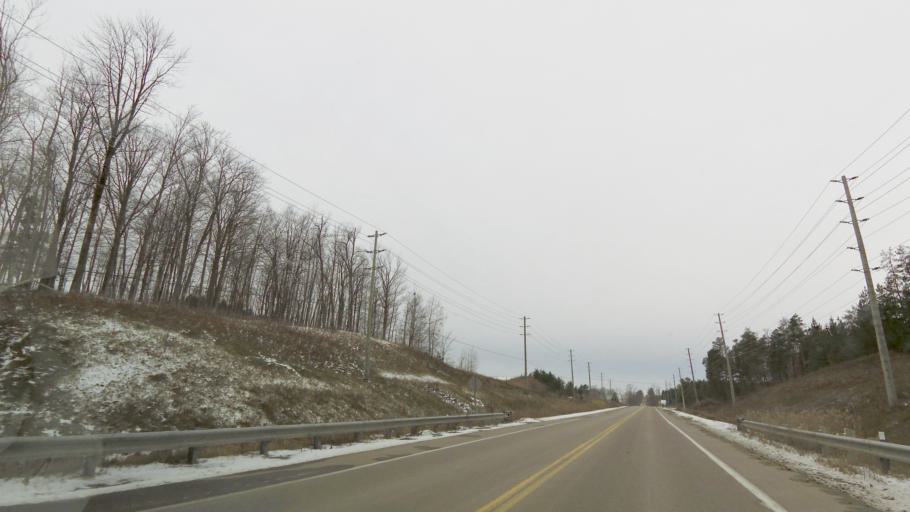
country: CA
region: Ontario
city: Newmarket
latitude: 44.0668
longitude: -79.5135
